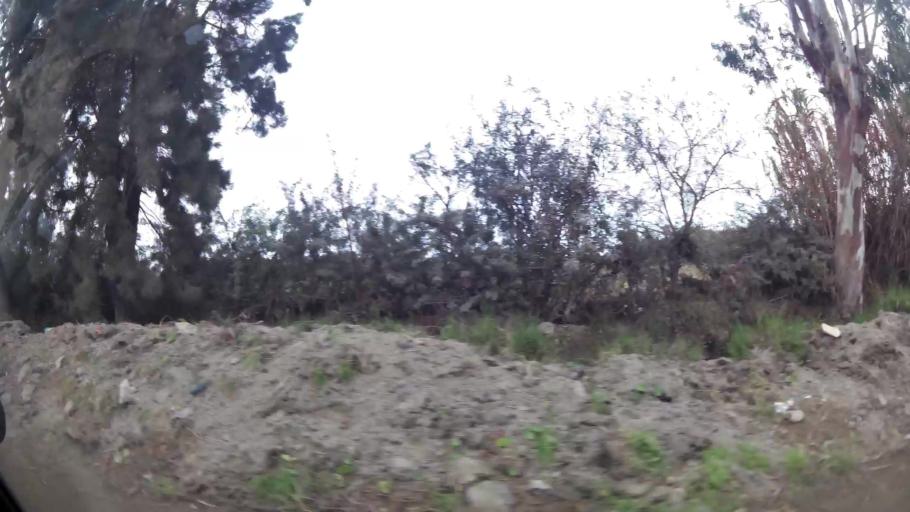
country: PE
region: Ica
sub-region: Provincia de Pisco
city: Pisco
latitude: -13.7344
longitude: -76.1989
